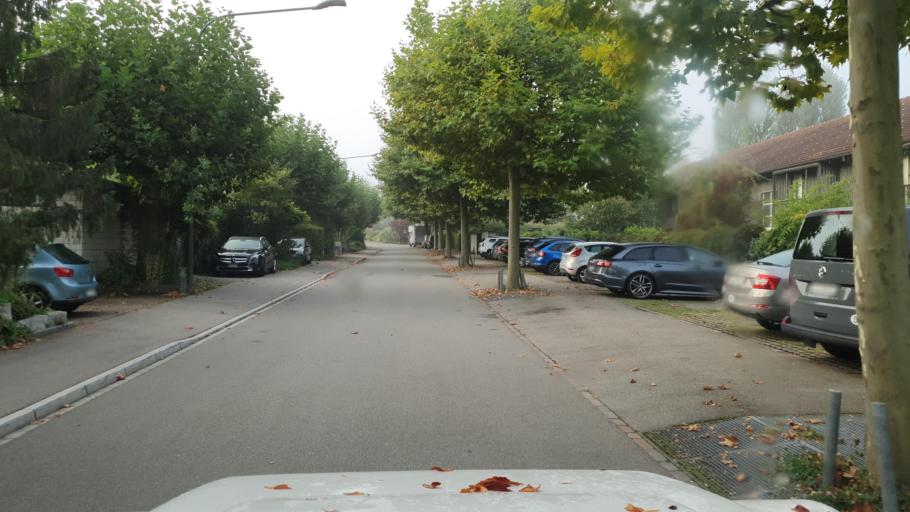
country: CH
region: Aargau
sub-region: Bezirk Baden
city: Mellingen
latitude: 47.4368
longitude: 8.2639
